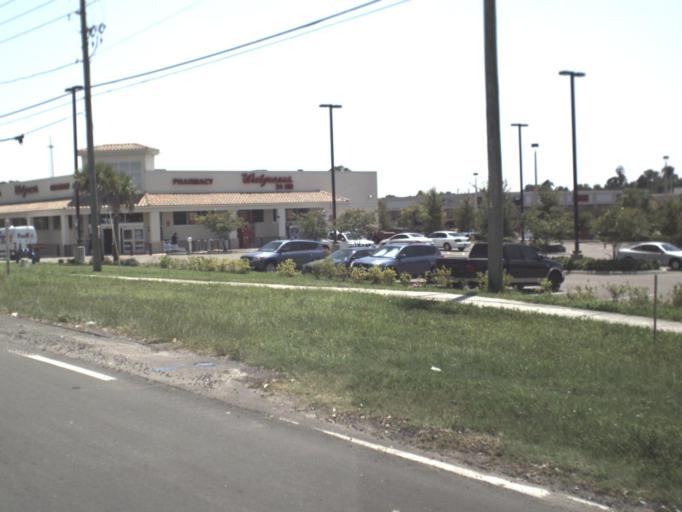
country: US
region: Florida
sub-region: Pinellas County
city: Saint George
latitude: 28.0487
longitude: -82.7387
